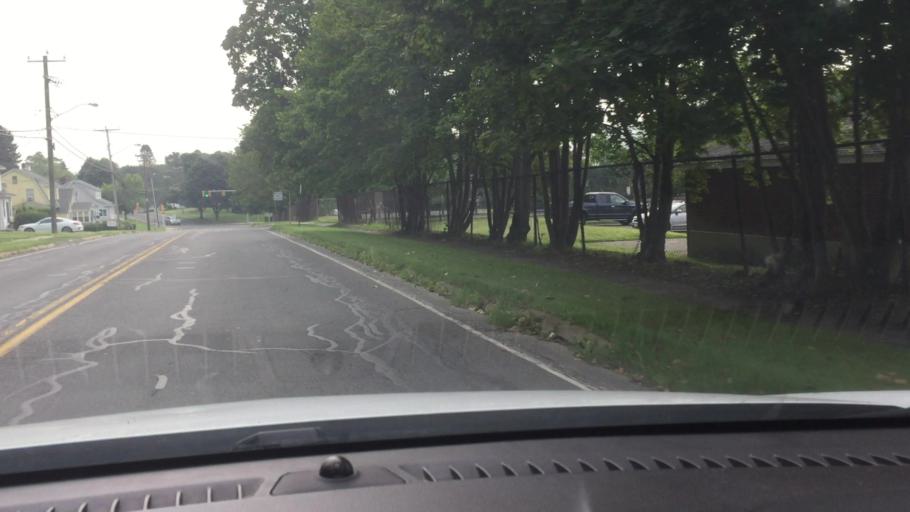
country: US
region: Massachusetts
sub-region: Berkshire County
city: Pittsfield
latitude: 42.4593
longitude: -73.2307
